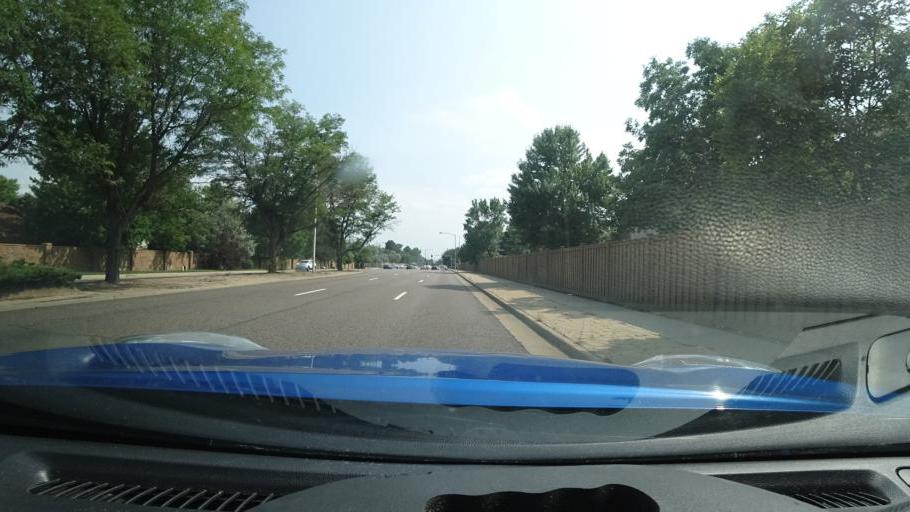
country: US
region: Colorado
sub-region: Adams County
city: Aurora
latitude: 39.6691
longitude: -104.8474
